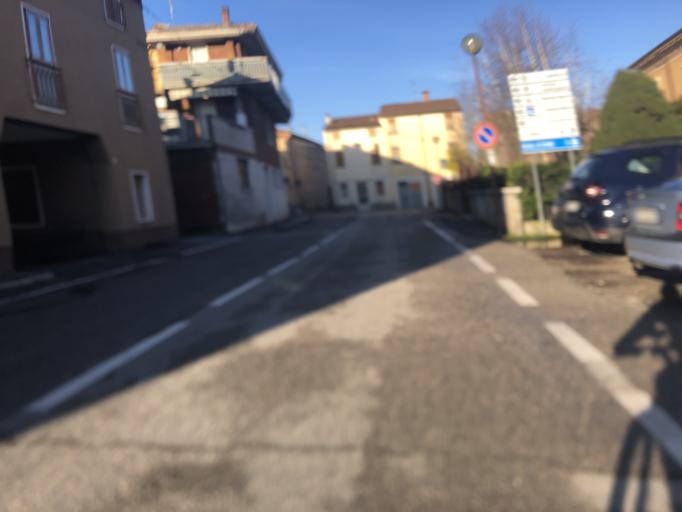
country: IT
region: Veneto
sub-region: Provincia di Verona
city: Pescantina
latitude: 45.4845
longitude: 10.8688
